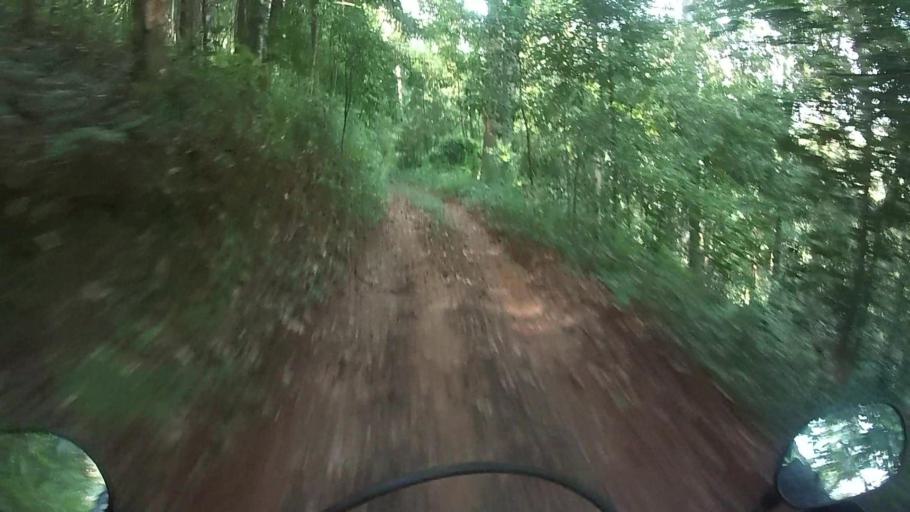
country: TH
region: Chiang Mai
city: Mae On
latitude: 19.0496
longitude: 99.2914
